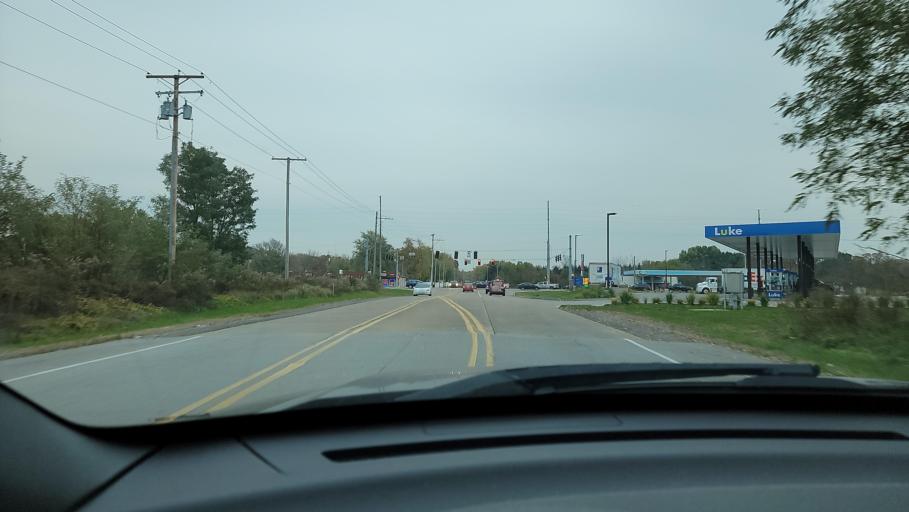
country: US
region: Indiana
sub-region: Lake County
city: Lake Station
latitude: 41.5517
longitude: -87.2215
